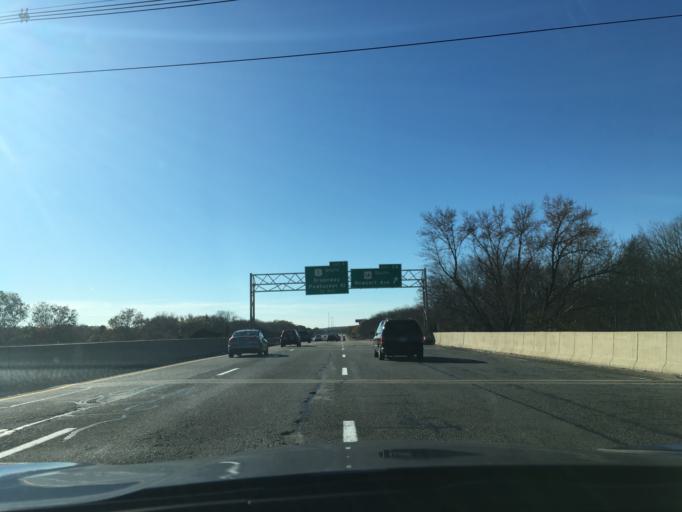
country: US
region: Massachusetts
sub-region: Bristol County
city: North Seekonk
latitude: 41.9028
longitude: -71.3554
